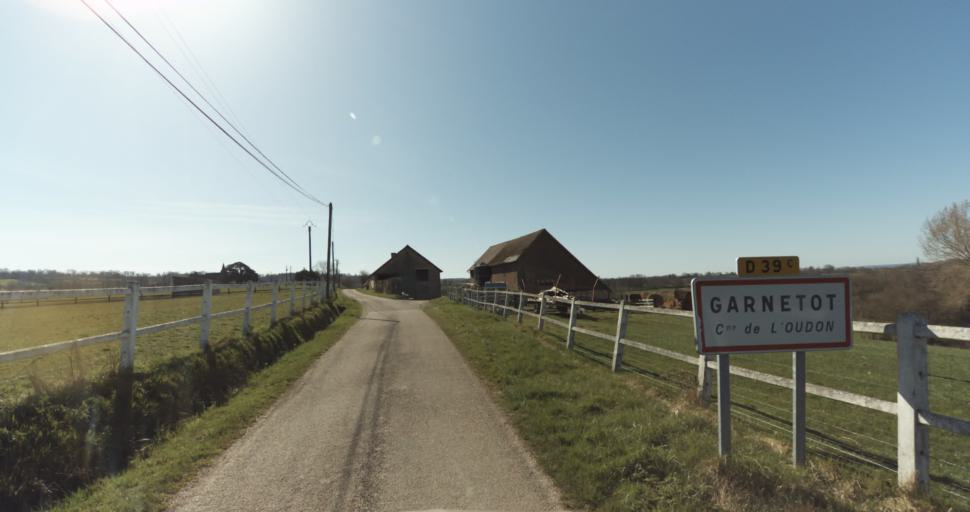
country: FR
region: Lower Normandy
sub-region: Departement de l'Orne
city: Trun
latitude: 48.9295
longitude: 0.0465
